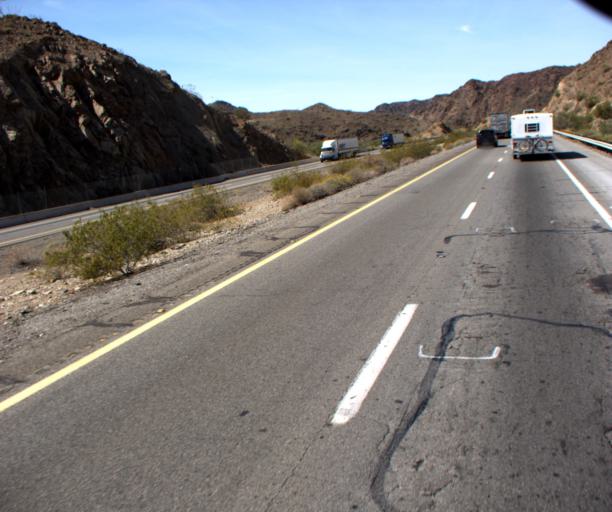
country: US
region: Arizona
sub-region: La Paz County
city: Quartzsite
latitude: 33.6485
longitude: -114.3640
